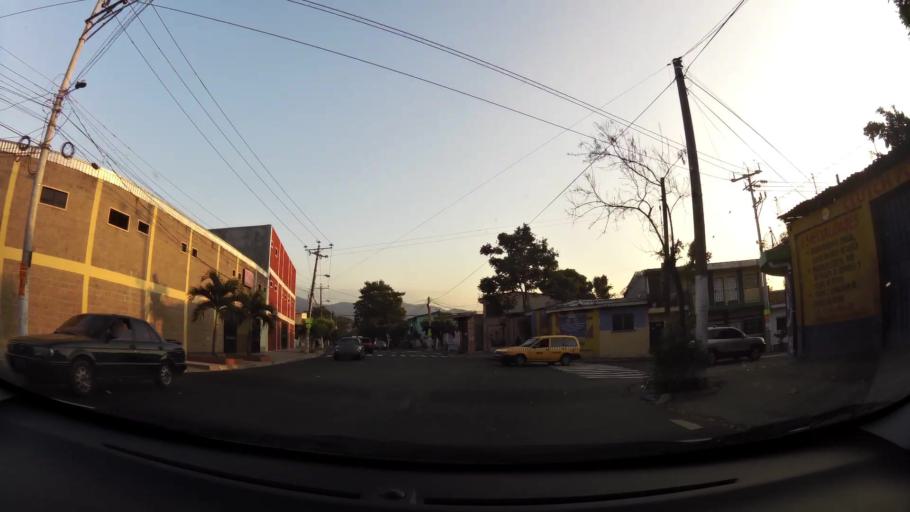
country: SV
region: San Salvador
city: Delgado
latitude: 13.7152
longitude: -89.1822
